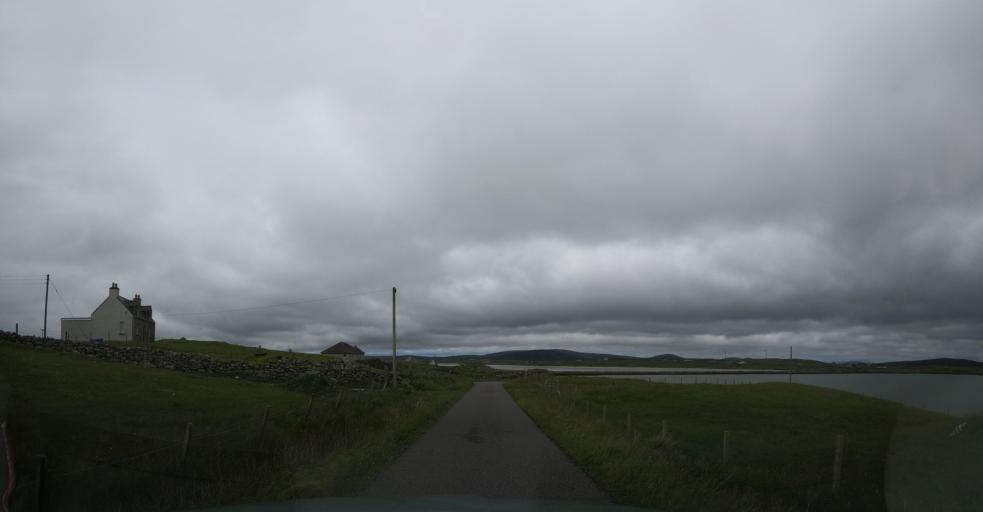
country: GB
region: Scotland
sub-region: Eilean Siar
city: Isle of North Uist
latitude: 57.5382
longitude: -7.3527
